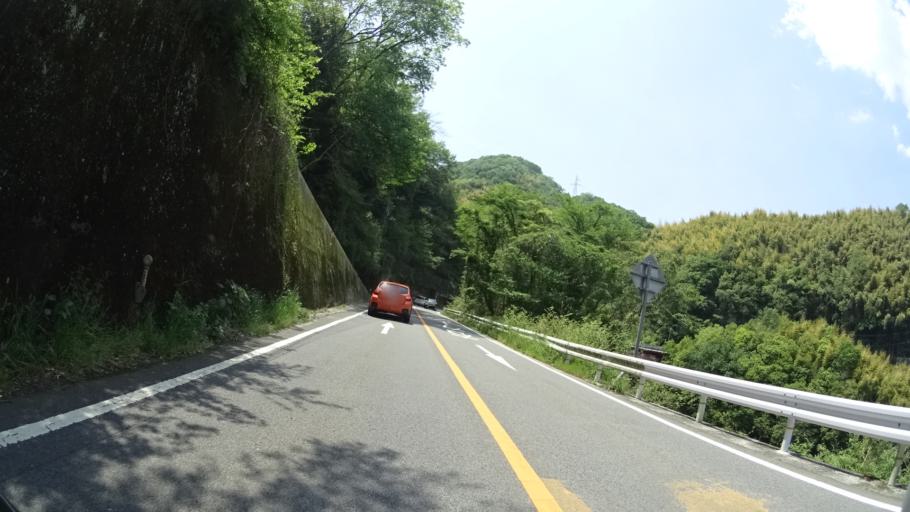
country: JP
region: Ehime
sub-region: Shikoku-chuo Shi
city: Matsuyama
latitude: 33.8825
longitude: 132.8368
